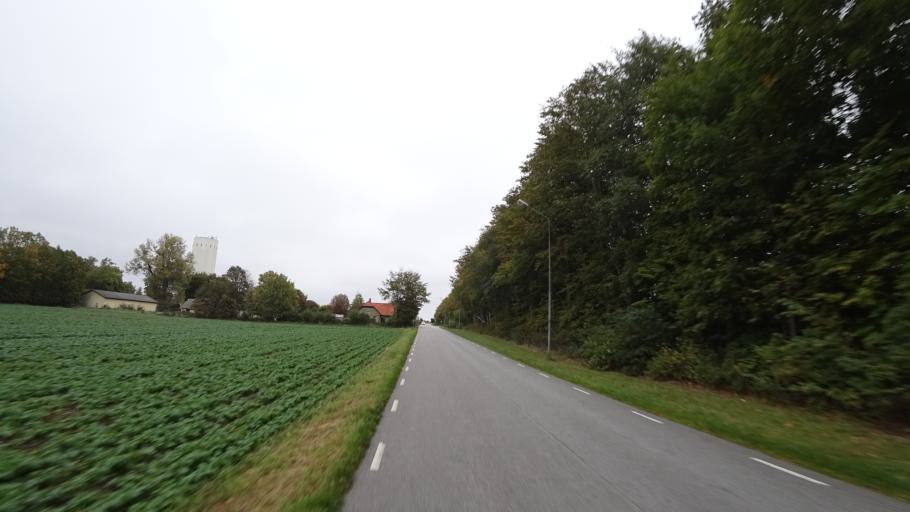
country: SE
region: Skane
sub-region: Kavlinge Kommun
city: Hofterup
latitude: 55.7736
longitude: 12.9525
